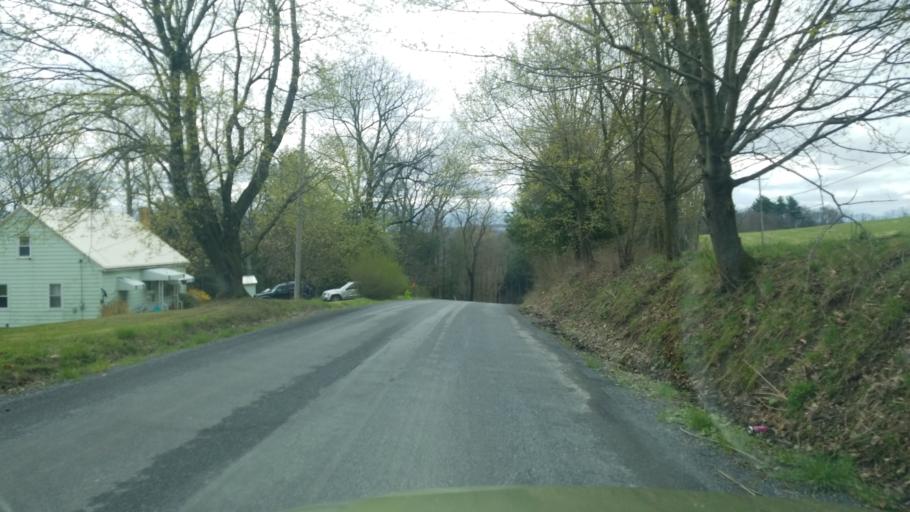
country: US
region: Pennsylvania
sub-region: Clearfield County
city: Clearfield
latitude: 41.0758
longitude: -78.3707
